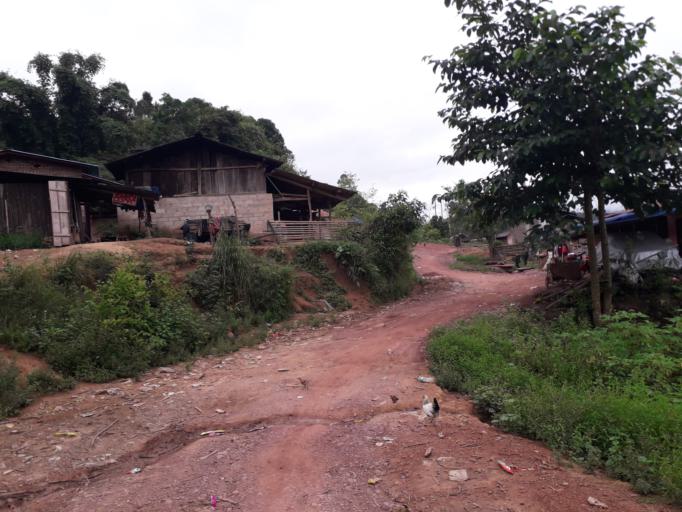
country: CN
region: Yunnan
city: Menglie
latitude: 22.2476
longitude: 101.6076
